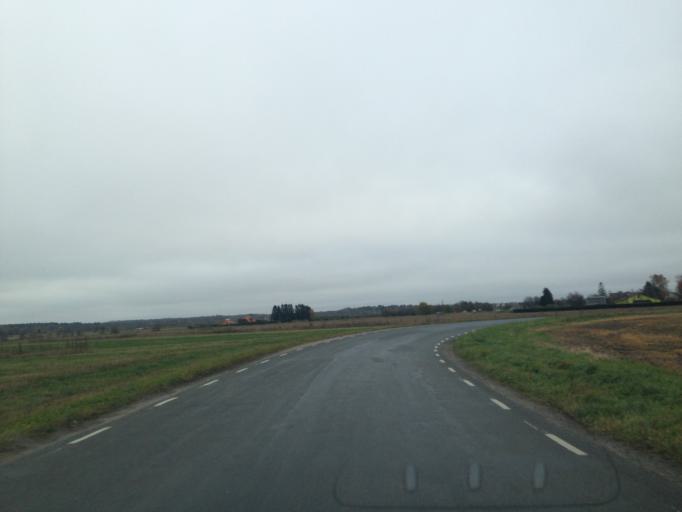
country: EE
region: Harju
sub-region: Saue linn
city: Saue
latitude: 59.3475
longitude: 24.5582
